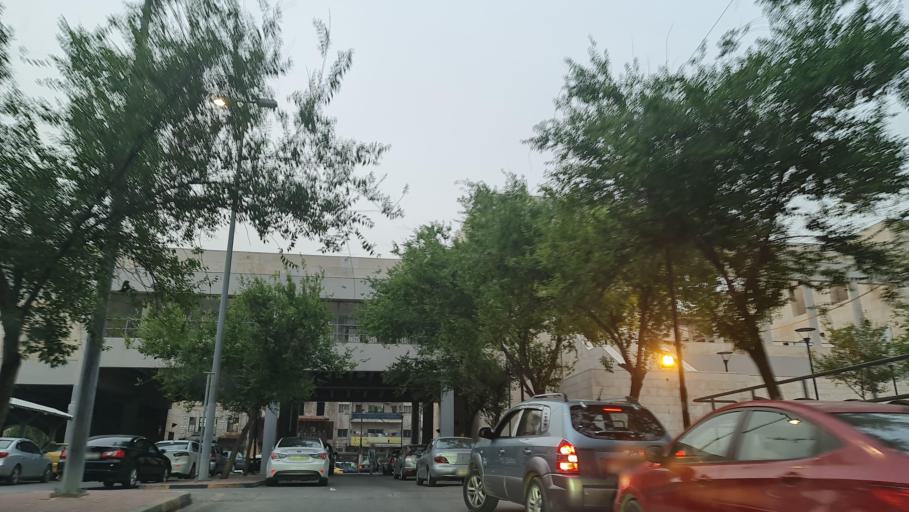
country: JO
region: Amman
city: Amman
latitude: 31.9524
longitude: 35.9428
